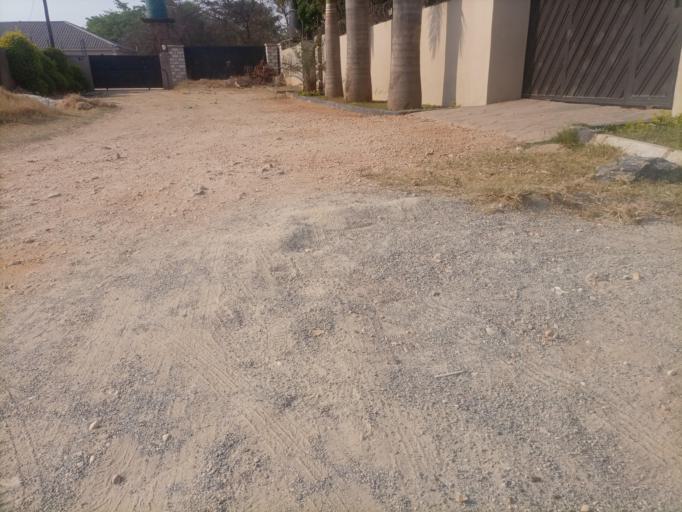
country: ZM
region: Lusaka
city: Lusaka
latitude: -15.4003
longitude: 28.3882
